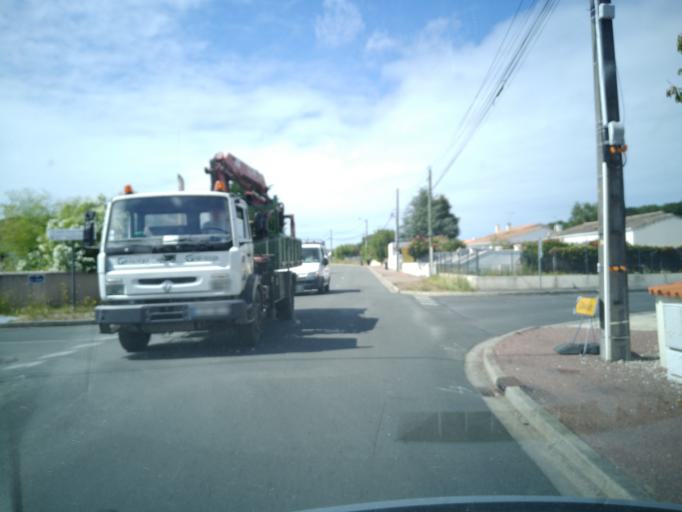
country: FR
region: Poitou-Charentes
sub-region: Departement de la Charente-Maritime
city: Vaux-sur-Mer
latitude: 45.6611
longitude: -1.0732
